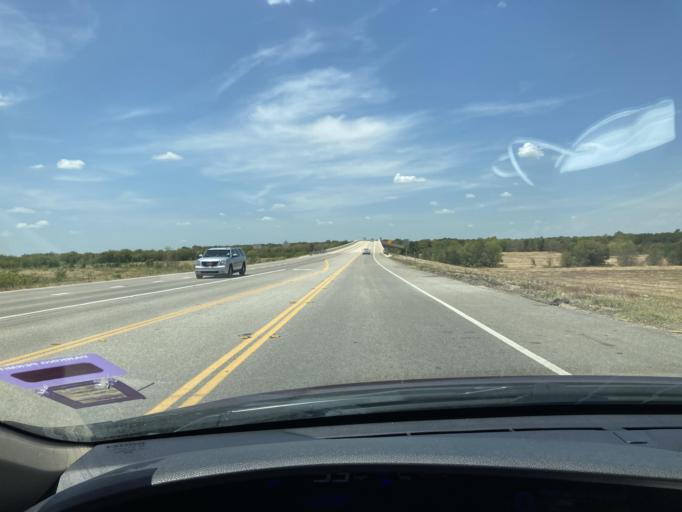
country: US
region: Texas
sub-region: Navarro County
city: Corsicana
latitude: 32.0424
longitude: -96.4486
